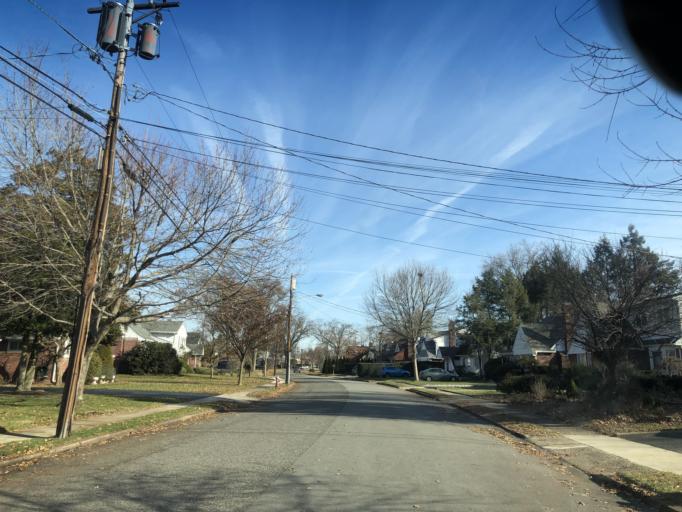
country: US
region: New Jersey
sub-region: Bergen County
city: Fair Lawn
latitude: 40.9252
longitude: -74.1263
